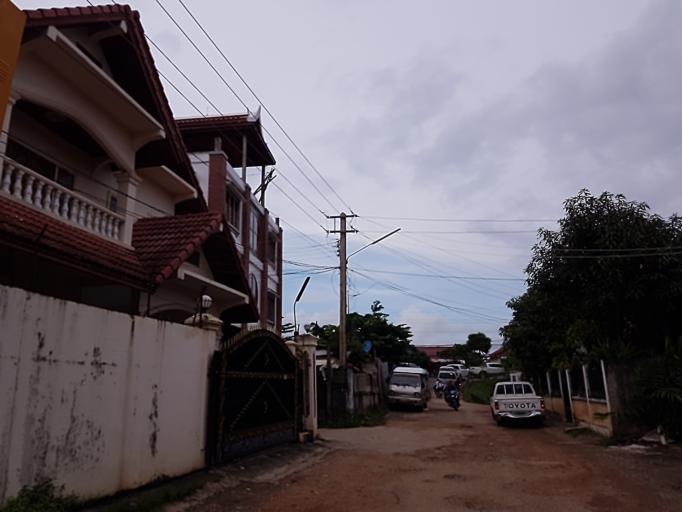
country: LA
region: Vientiane
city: Vientiane
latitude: 17.9513
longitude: 102.6234
